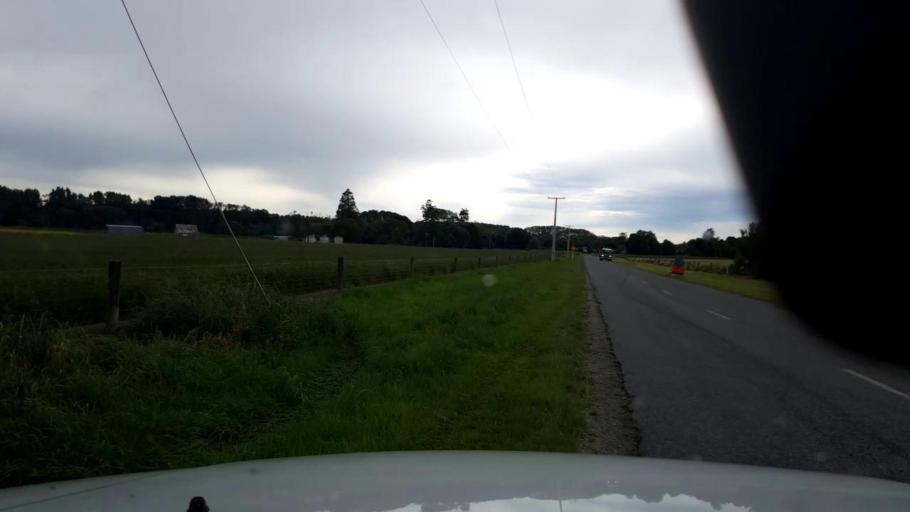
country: NZ
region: Canterbury
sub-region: Timaru District
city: Pleasant Point
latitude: -44.2697
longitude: 171.2590
